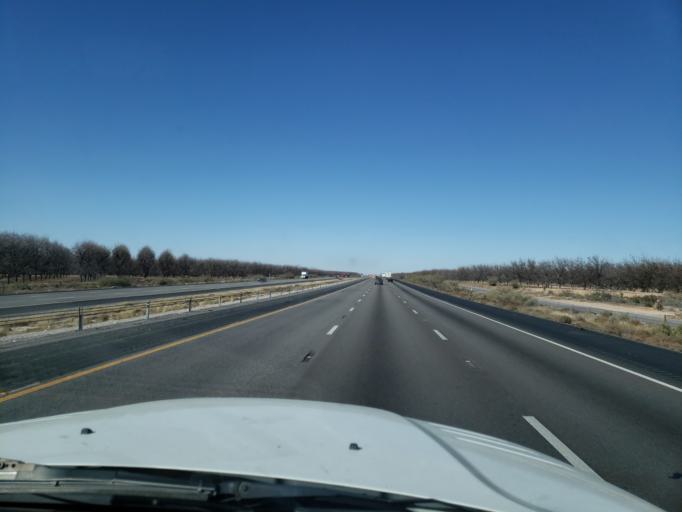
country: US
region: New Mexico
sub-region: Dona Ana County
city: Mesquite
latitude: 32.2253
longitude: -106.7067
